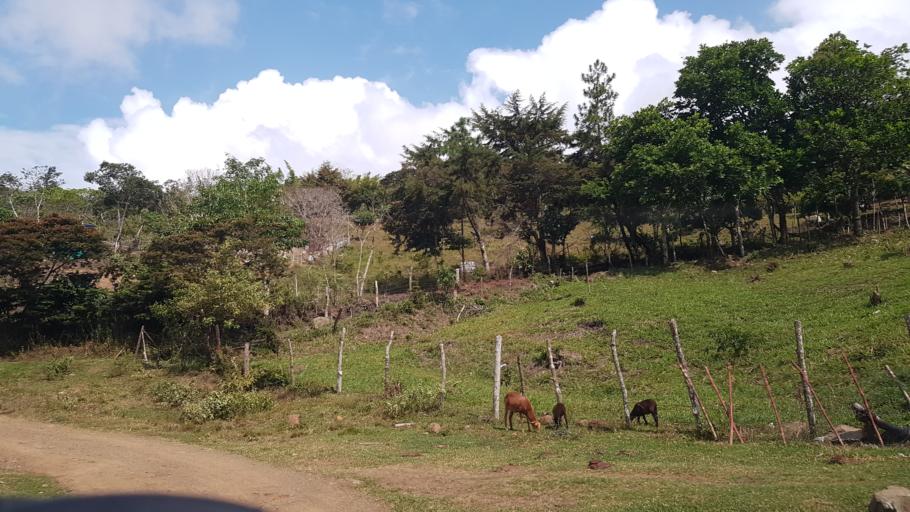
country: CO
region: Valle del Cauca
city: Yumbo
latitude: 3.6535
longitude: -76.5155
